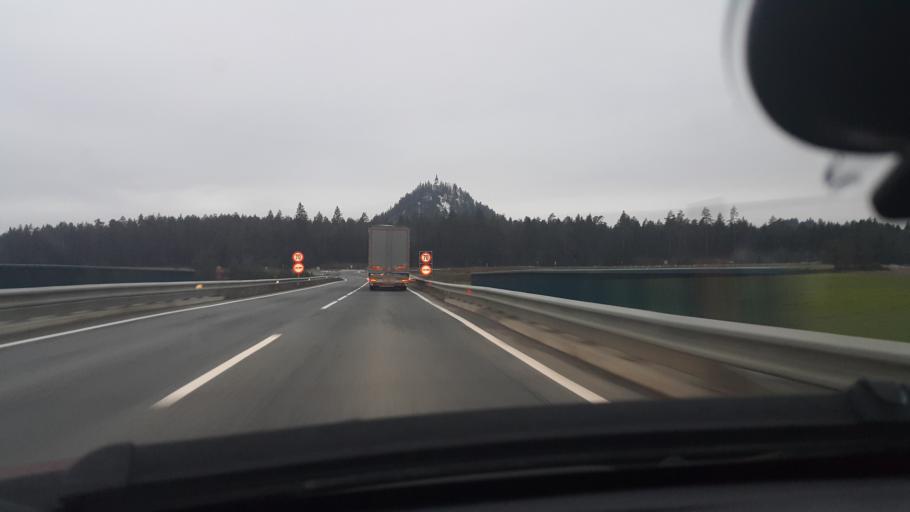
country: AT
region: Carinthia
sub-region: Politischer Bezirk Volkermarkt
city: Ruden
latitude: 46.6597
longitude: 14.7657
